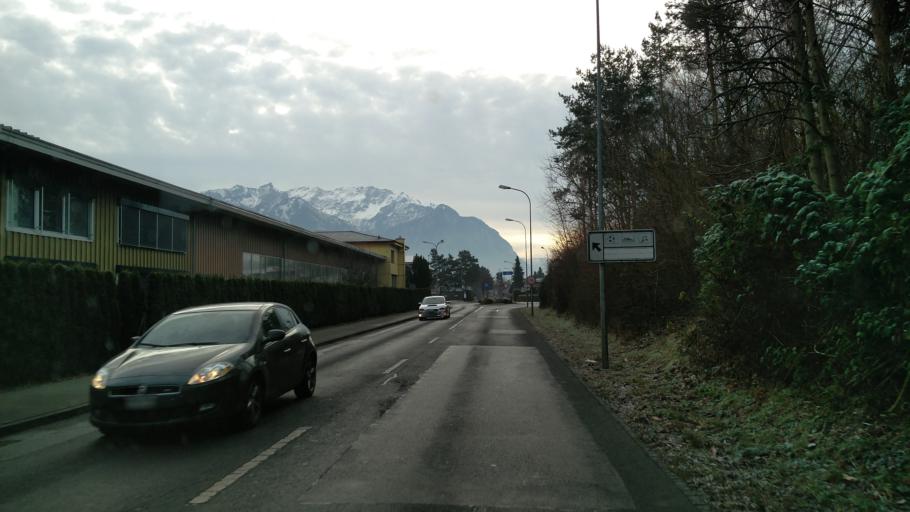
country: CH
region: Saint Gallen
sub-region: Wahlkreis Werdenberg
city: Buchs
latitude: 47.1613
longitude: 9.4790
